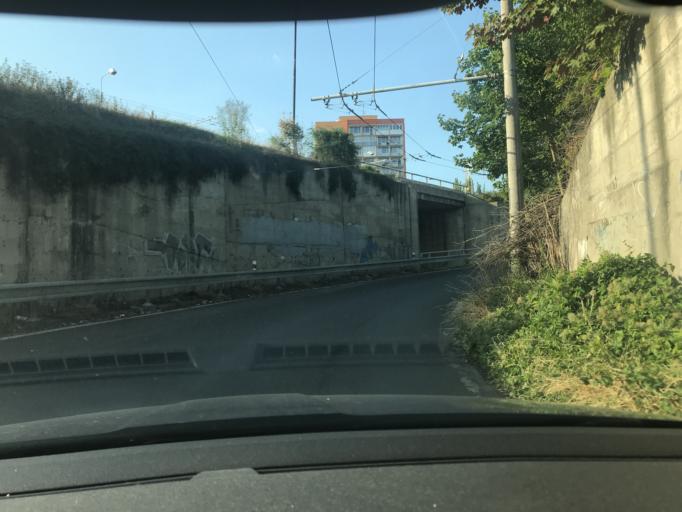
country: CZ
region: Ustecky
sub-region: Okres Chomutov
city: Chomutov
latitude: 50.4637
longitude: 13.4050
